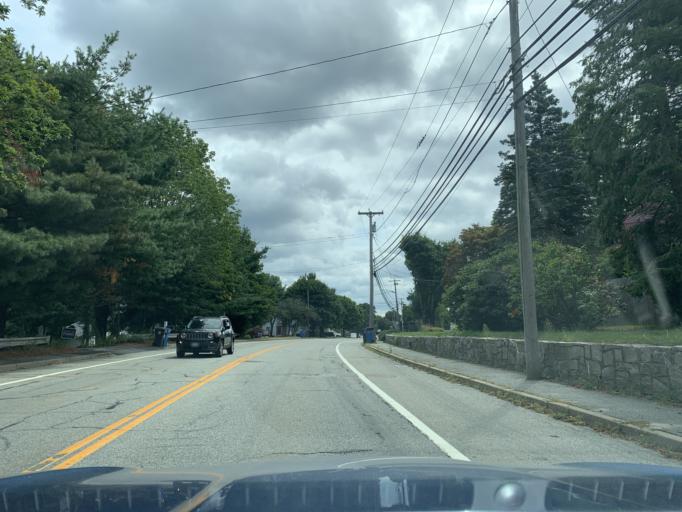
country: US
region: Rhode Island
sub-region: Providence County
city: Johnston
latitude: 41.7803
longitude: -71.4922
